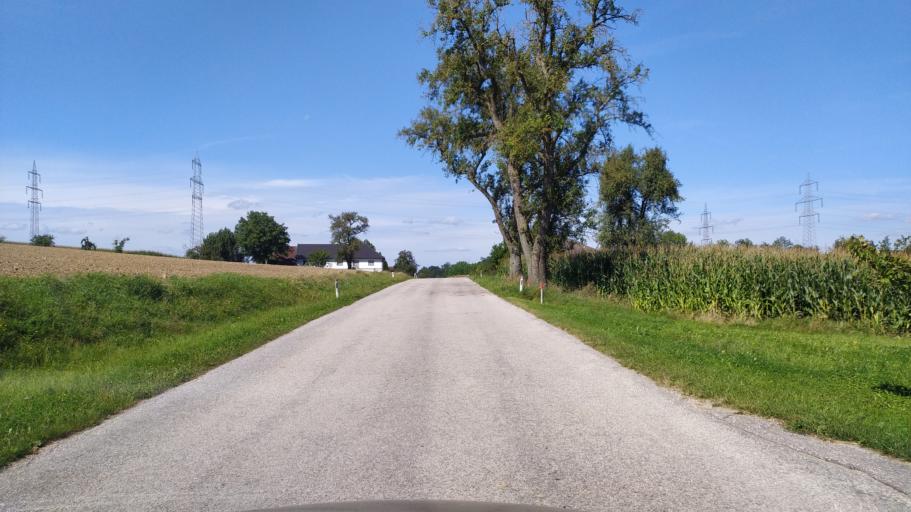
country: AT
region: Lower Austria
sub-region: Politischer Bezirk Amstetten
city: Strengberg
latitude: 48.1305
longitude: 14.6728
